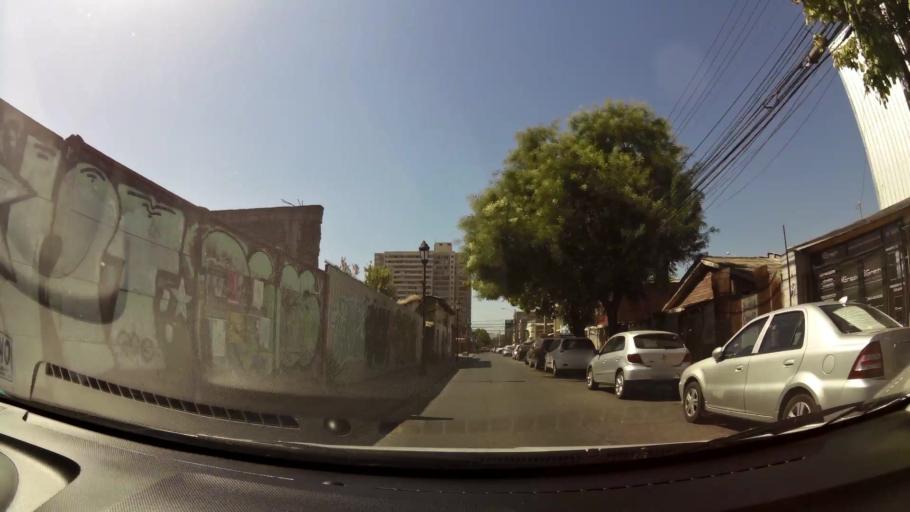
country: CL
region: Maule
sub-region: Provincia de Talca
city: Talca
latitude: -35.4306
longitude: -71.6586
